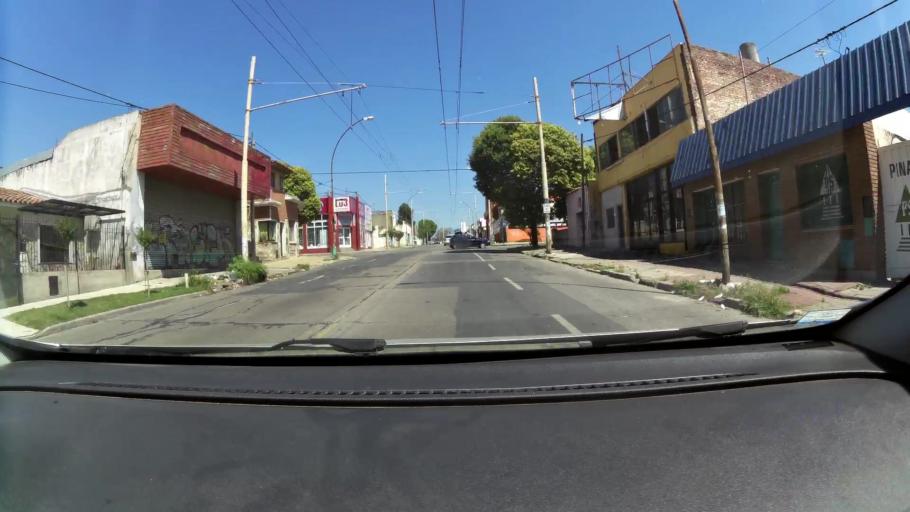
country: AR
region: Cordoba
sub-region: Departamento de Capital
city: Cordoba
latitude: -31.4281
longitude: -64.2059
